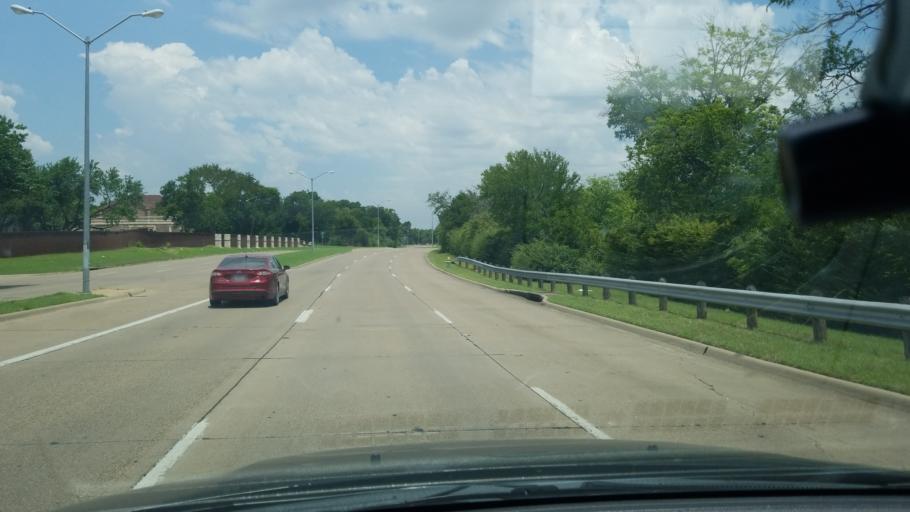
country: US
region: Texas
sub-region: Dallas County
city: Balch Springs
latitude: 32.7249
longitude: -96.6660
